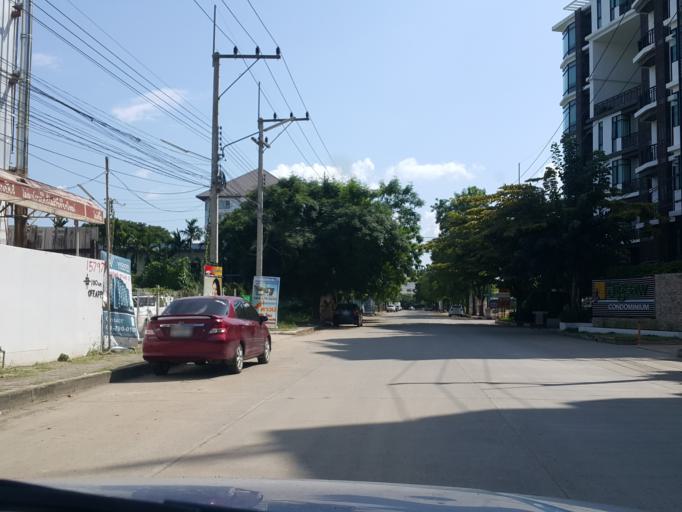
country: TH
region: Chiang Mai
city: Chiang Mai
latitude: 18.7975
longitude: 99.0257
